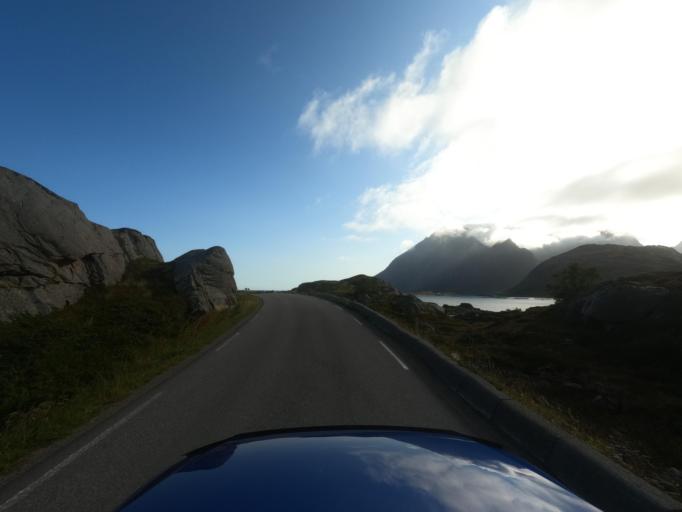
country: NO
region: Nordland
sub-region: Flakstad
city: Ramberg
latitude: 68.0129
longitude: 13.1959
